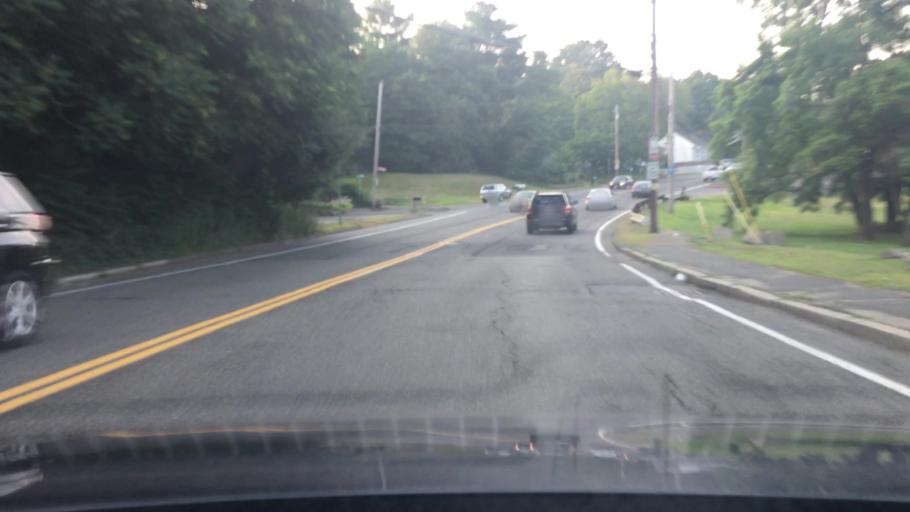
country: US
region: Massachusetts
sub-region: Essex County
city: Saugus
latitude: 42.4876
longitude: -71.0150
